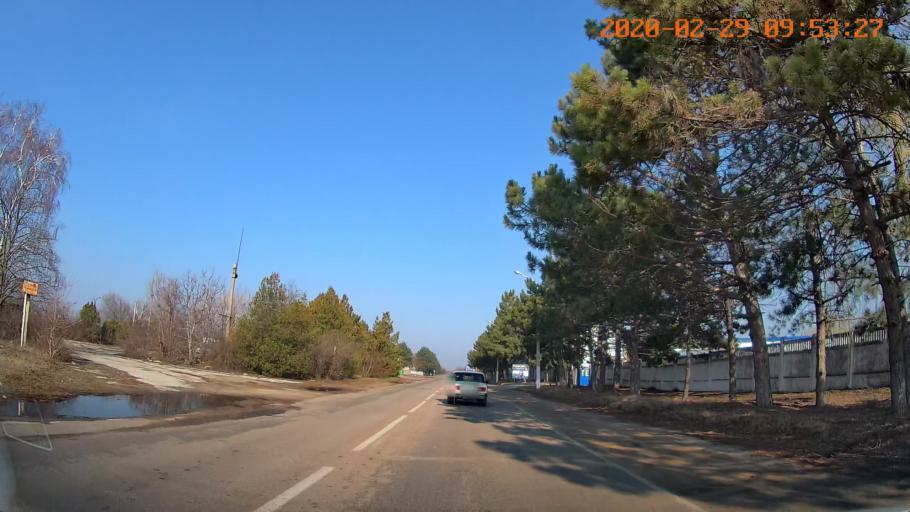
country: MD
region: Telenesti
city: Slobozia
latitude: 46.7221
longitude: 29.7216
